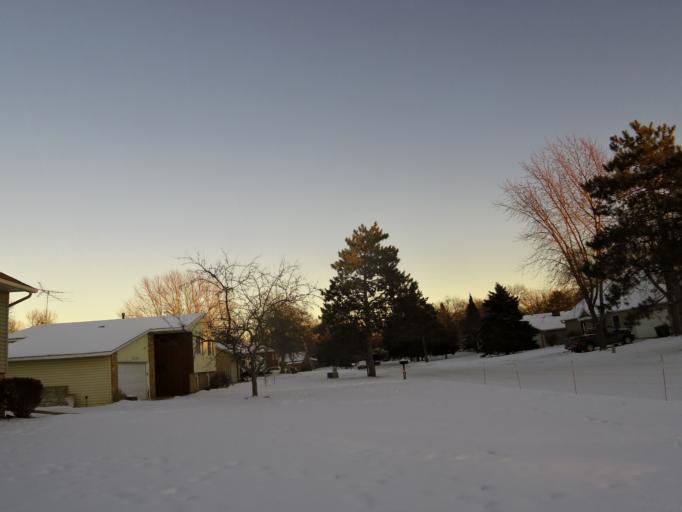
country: US
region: Minnesota
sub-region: Washington County
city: Stillwater
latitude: 45.0513
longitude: -92.8441
